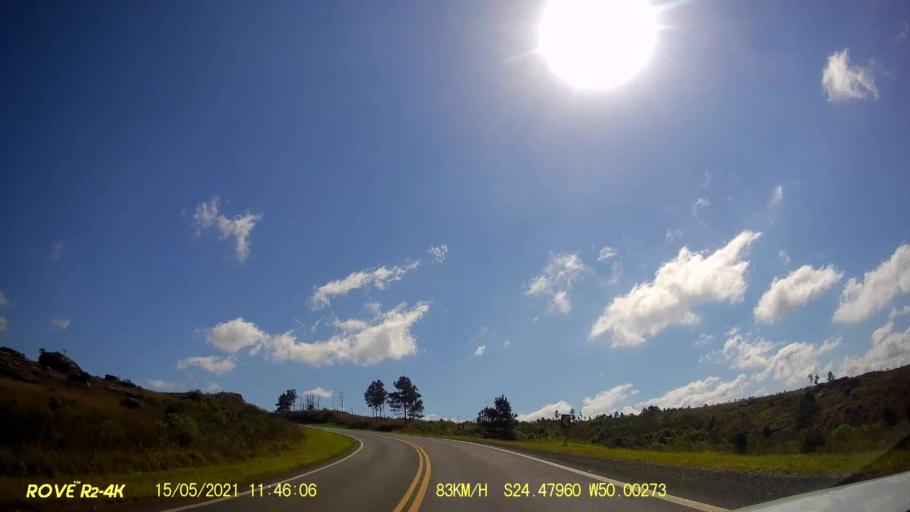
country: BR
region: Parana
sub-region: Pirai Do Sul
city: Pirai do Sul
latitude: -24.4793
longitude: -50.0031
